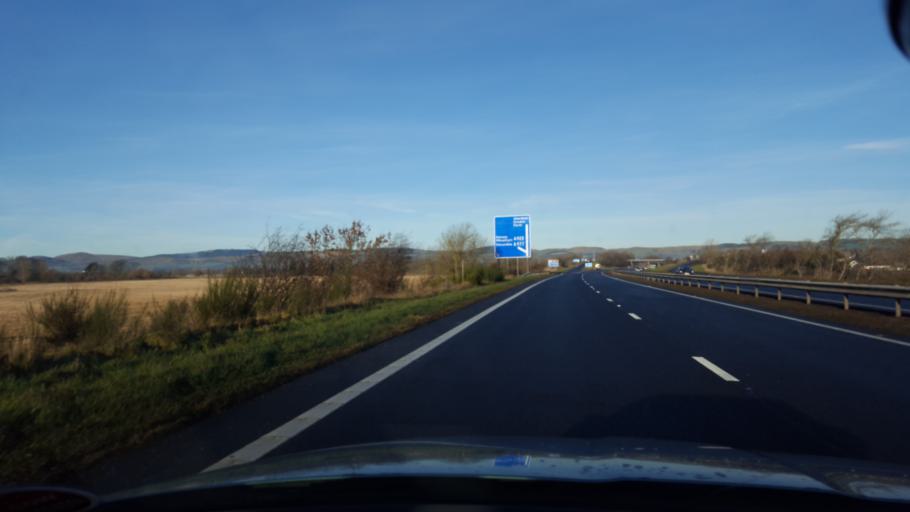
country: GB
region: Scotland
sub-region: Perth and Kinross
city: Kinross
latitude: 56.2021
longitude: -3.4319
